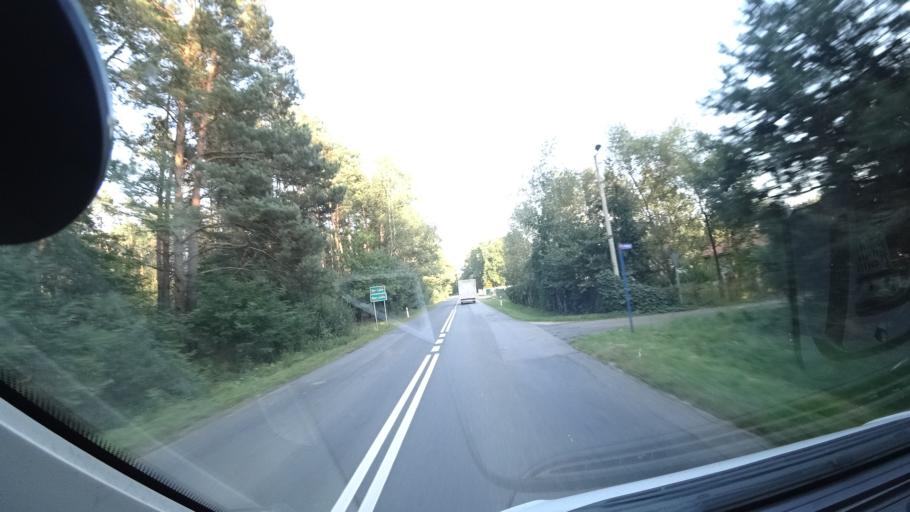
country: PL
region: Silesian Voivodeship
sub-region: Powiat gliwicki
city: Rudziniec
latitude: 50.2685
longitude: 18.4181
